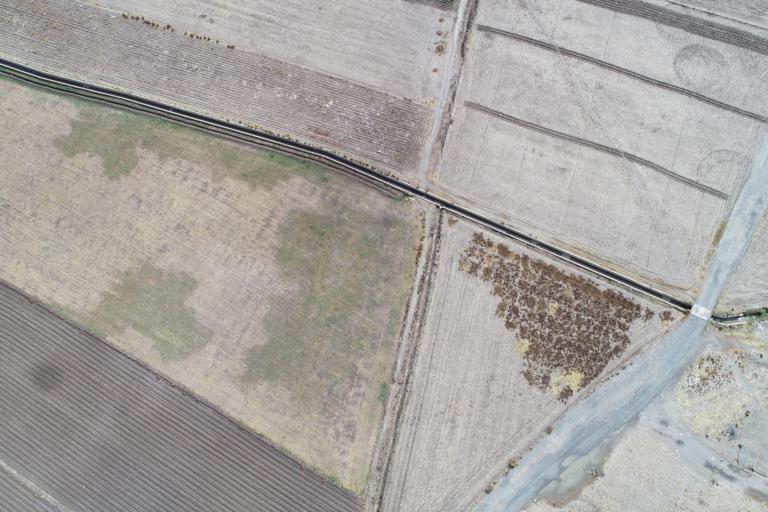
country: BO
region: La Paz
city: Achacachi
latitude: -16.0368
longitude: -68.6831
